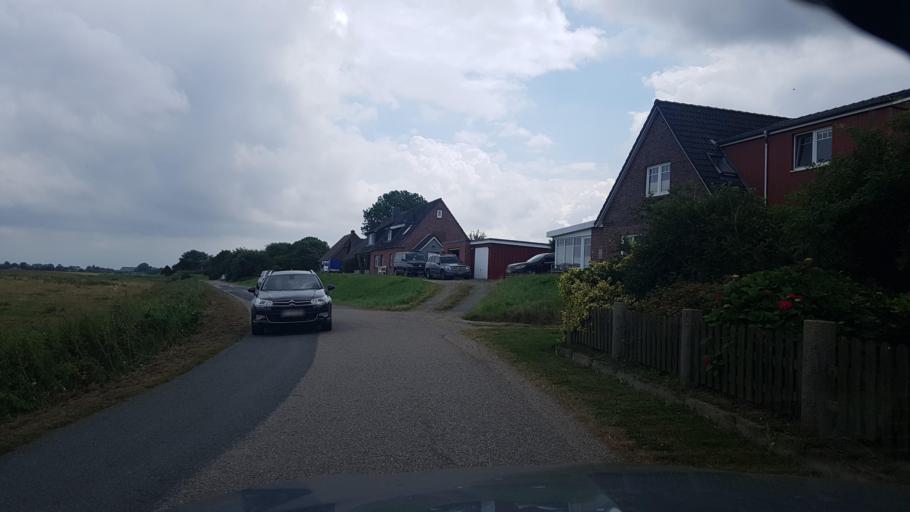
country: DE
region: Schleswig-Holstein
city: Elisabeth-Sophien-Koog
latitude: 54.4823
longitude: 8.8278
